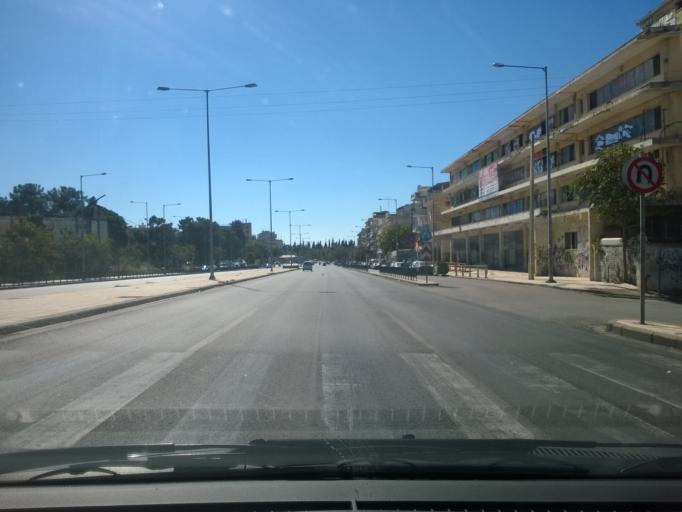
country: GR
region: Central Macedonia
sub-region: Nomos Thessalonikis
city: Stavroupoli
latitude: 40.6599
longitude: 22.9351
